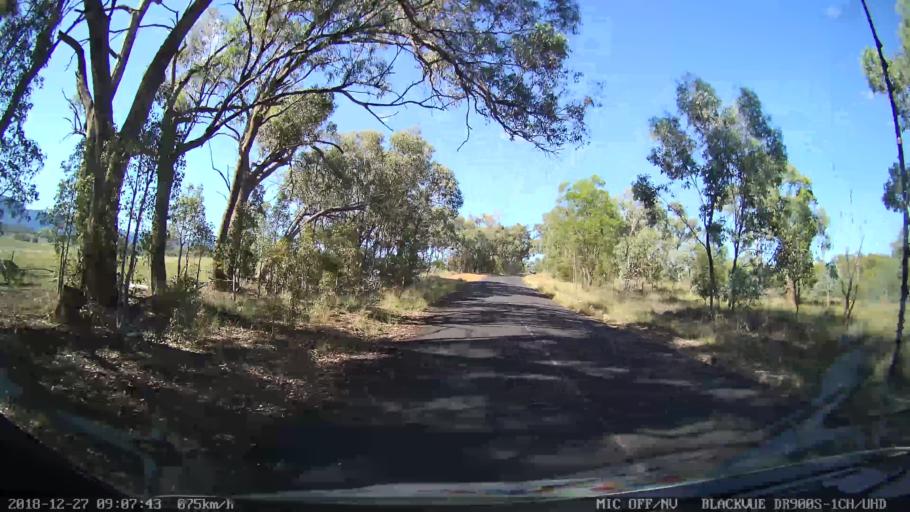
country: AU
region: New South Wales
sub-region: Lithgow
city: Portland
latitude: -33.1312
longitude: 150.1551
